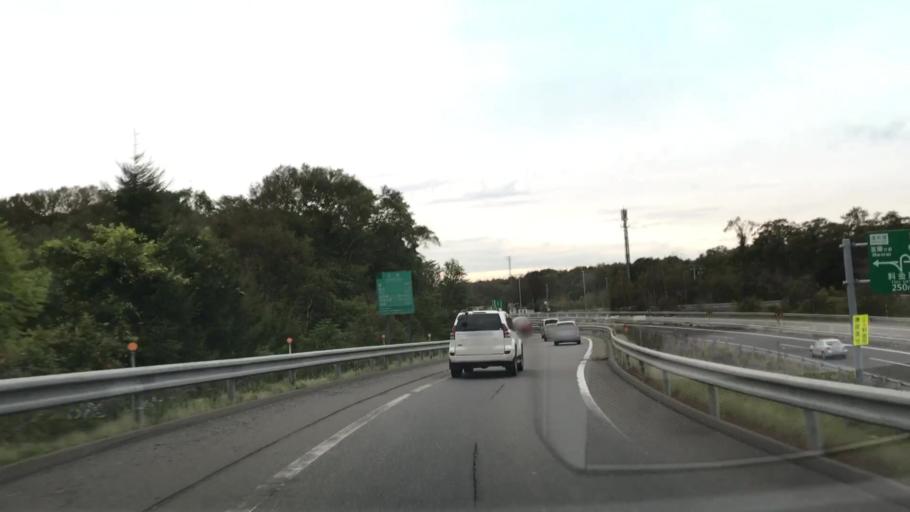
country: JP
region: Hokkaido
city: Tomakomai
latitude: 42.7082
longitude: 141.6585
